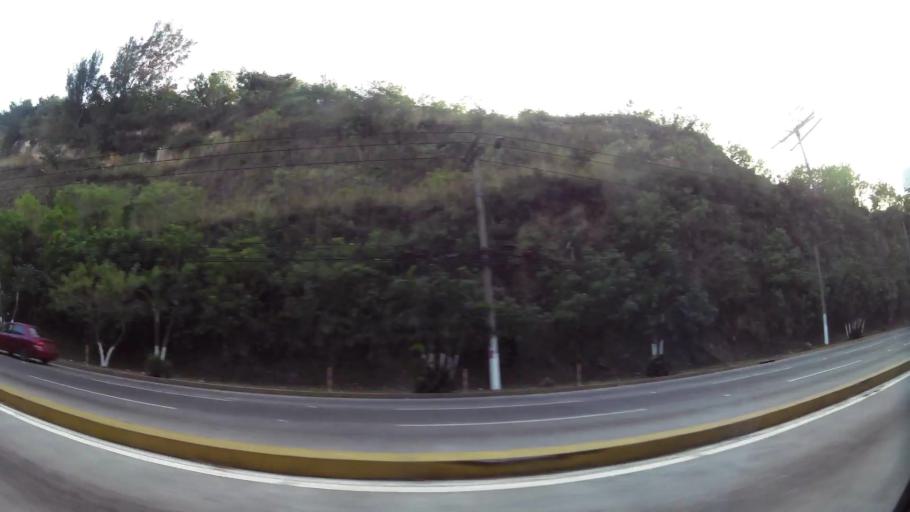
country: SV
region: San Salvador
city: San Salvador
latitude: 13.6827
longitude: -89.2172
